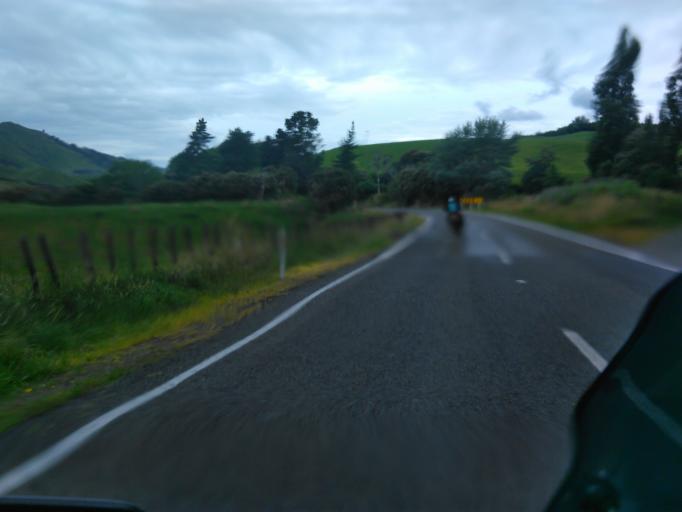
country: NZ
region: Gisborne
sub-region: Gisborne District
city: Gisborne
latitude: -38.4531
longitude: 177.6310
